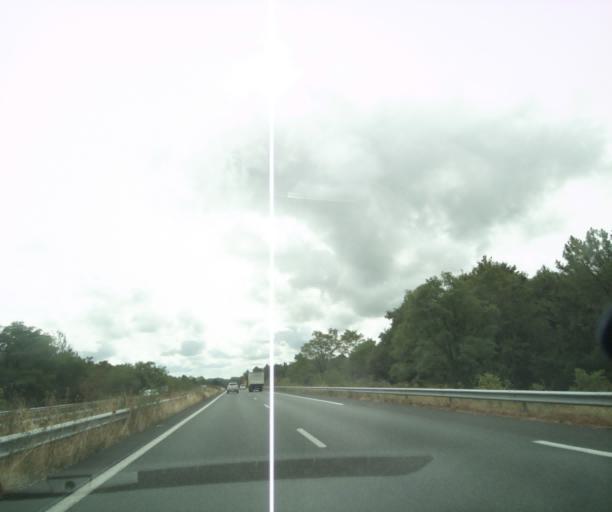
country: FR
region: Poitou-Charentes
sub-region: Departement de la Charente-Maritime
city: Mirambeau
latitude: 45.3488
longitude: -0.5795
